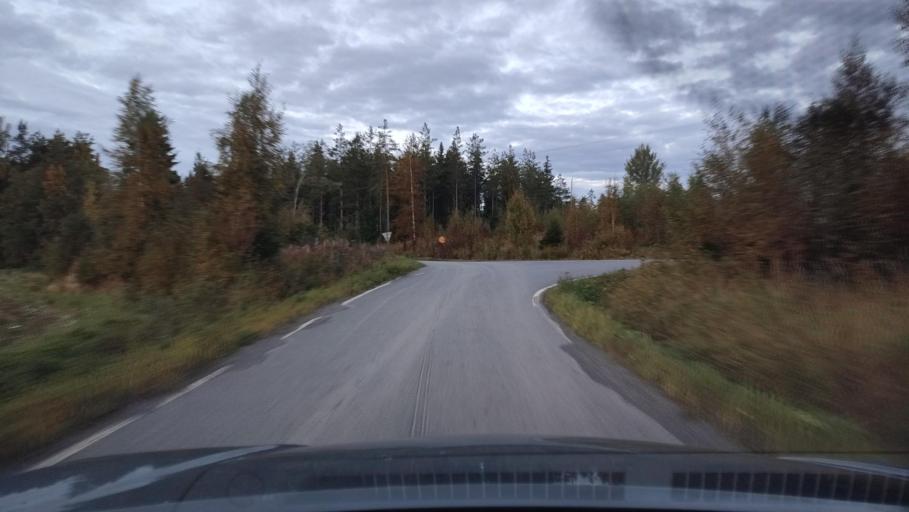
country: FI
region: Ostrobothnia
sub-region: Sydosterbotten
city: Kristinestad
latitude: 62.2759
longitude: 21.5152
